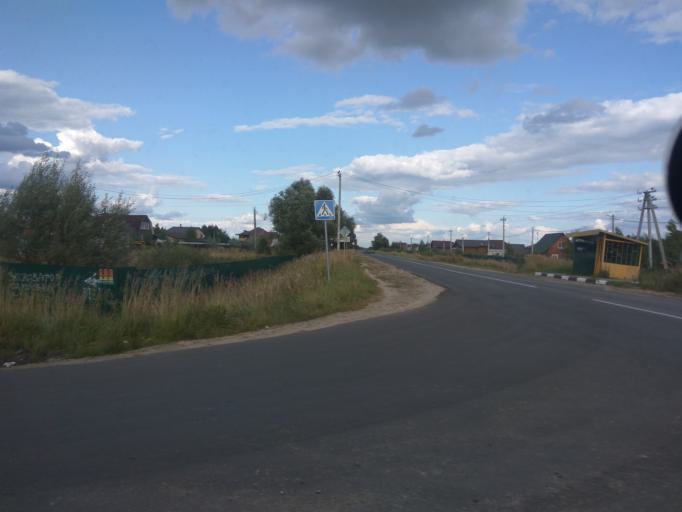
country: RU
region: Moskovskaya
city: Bronnitsy
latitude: 55.4553
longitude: 38.2727
